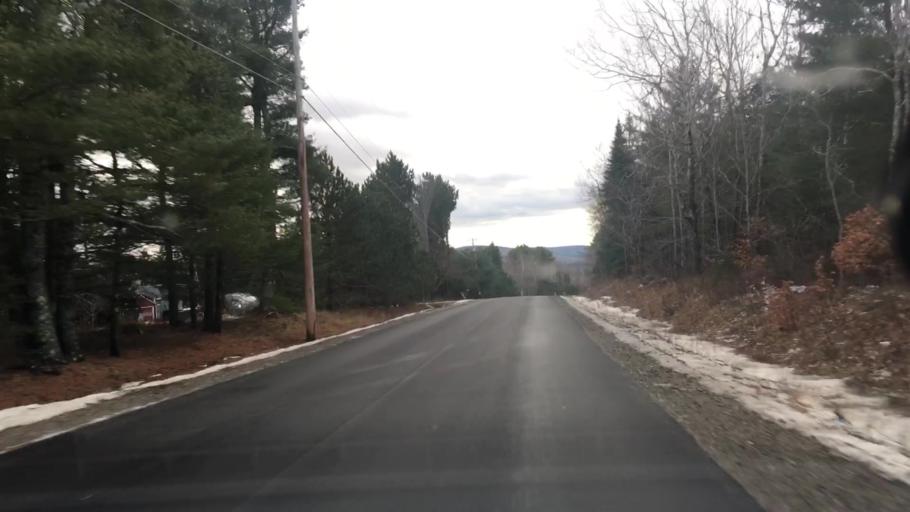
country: US
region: Maine
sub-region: Hancock County
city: Dedham
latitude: 44.6582
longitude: -68.7047
